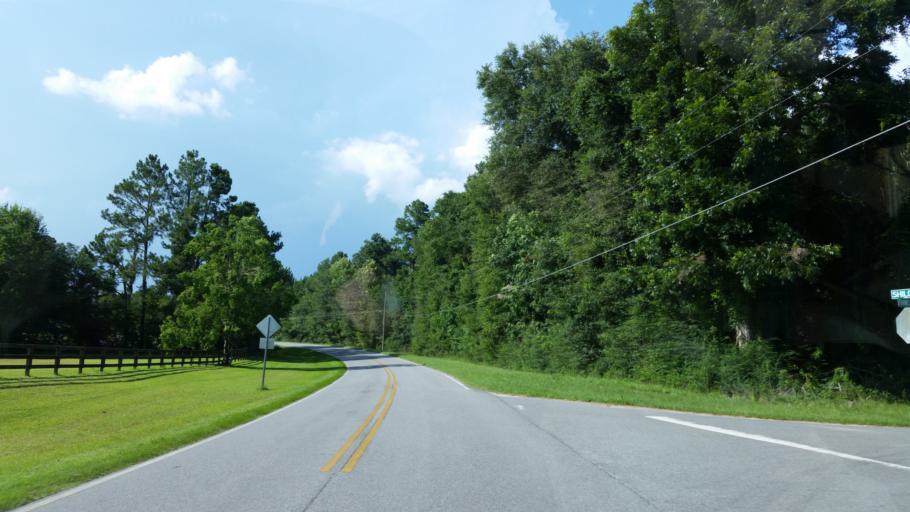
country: US
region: Georgia
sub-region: Lowndes County
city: Hahira
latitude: 30.9399
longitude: -83.4081
